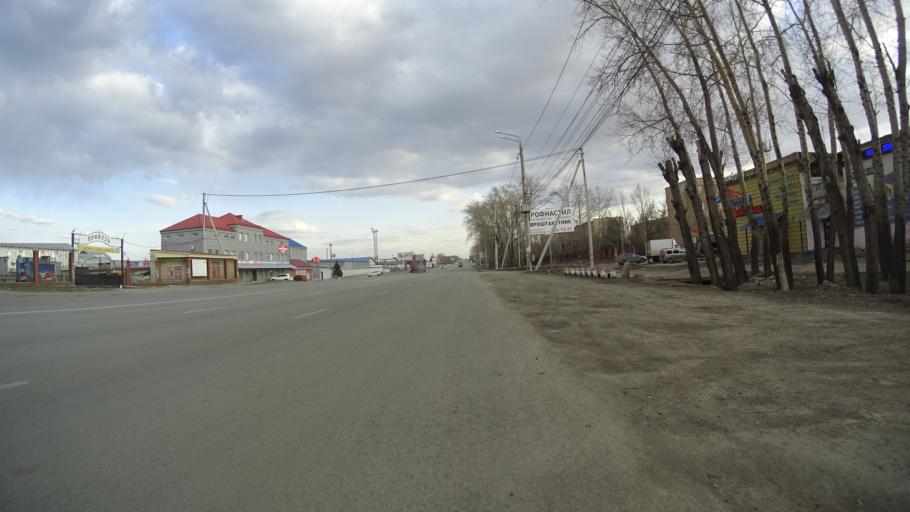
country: RU
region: Chelyabinsk
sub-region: Gorod Chelyabinsk
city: Chelyabinsk
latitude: 55.1099
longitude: 61.3867
